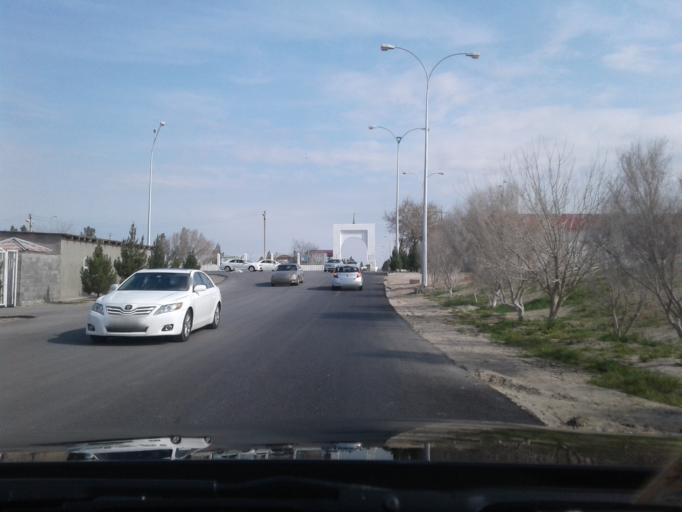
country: TM
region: Ahal
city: Ashgabat
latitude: 38.0959
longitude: 58.3854
